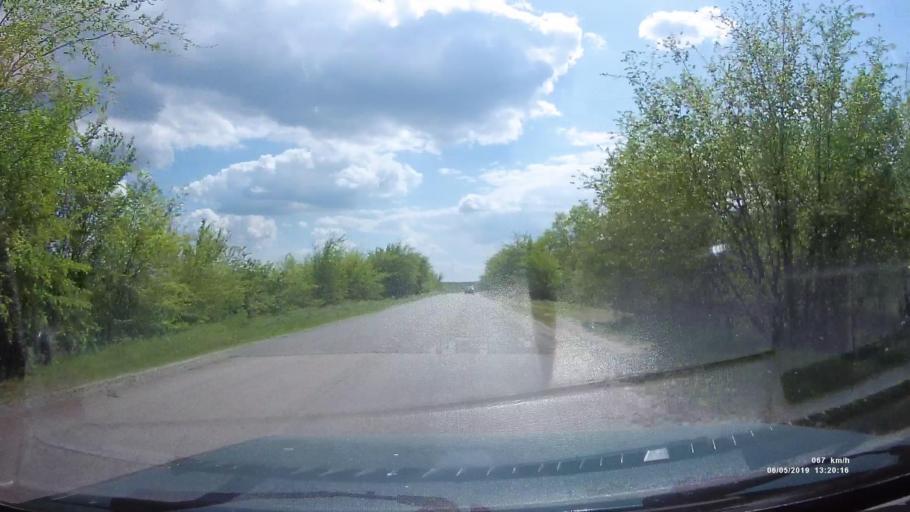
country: RU
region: Rostov
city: Ust'-Donetskiy
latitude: 47.7179
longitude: 40.9114
